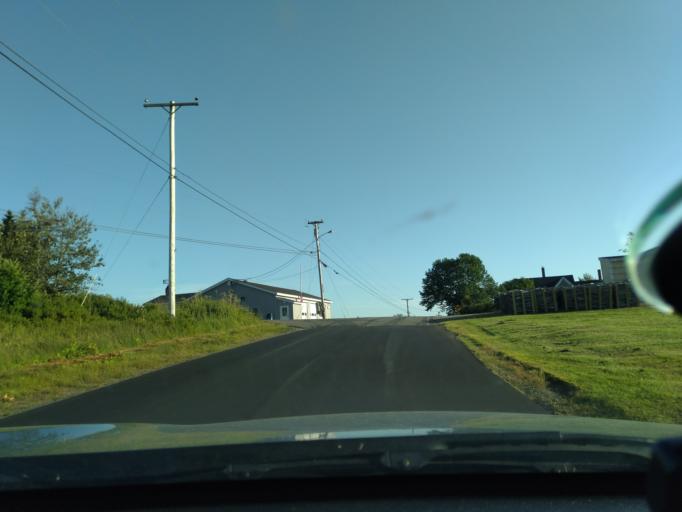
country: US
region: Maine
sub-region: Washington County
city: Machiasport
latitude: 44.6590
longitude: -67.2031
